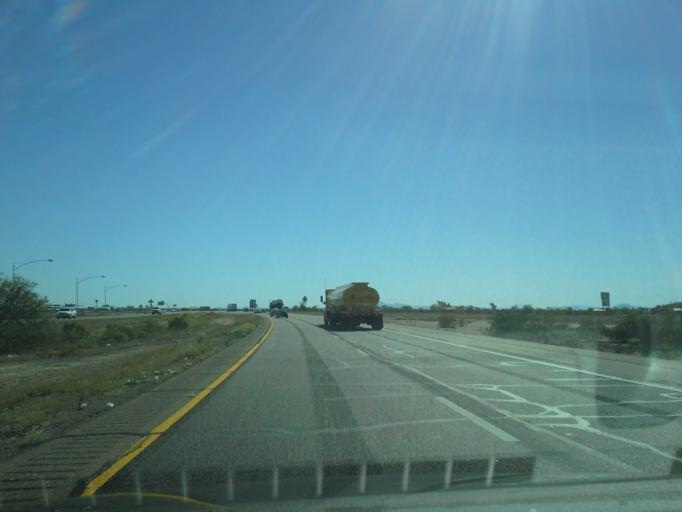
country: US
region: Arizona
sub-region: Pinal County
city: Arizona City
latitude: 32.8185
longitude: -111.6831
